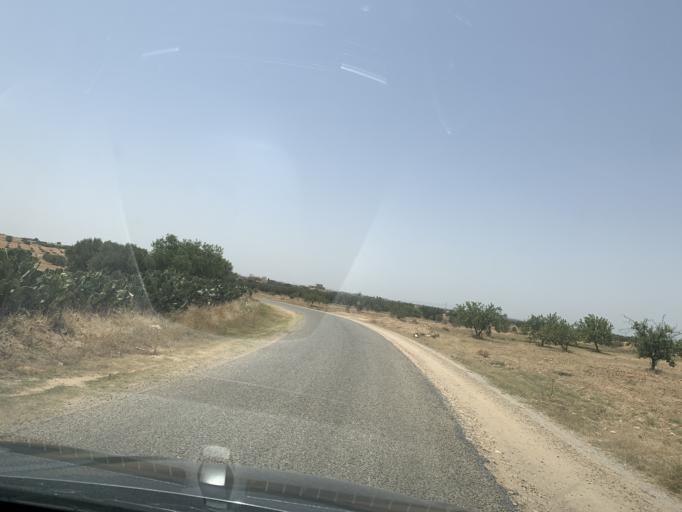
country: TN
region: Al Mahdiyah
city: Shurban
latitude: 35.1629
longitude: 10.2449
